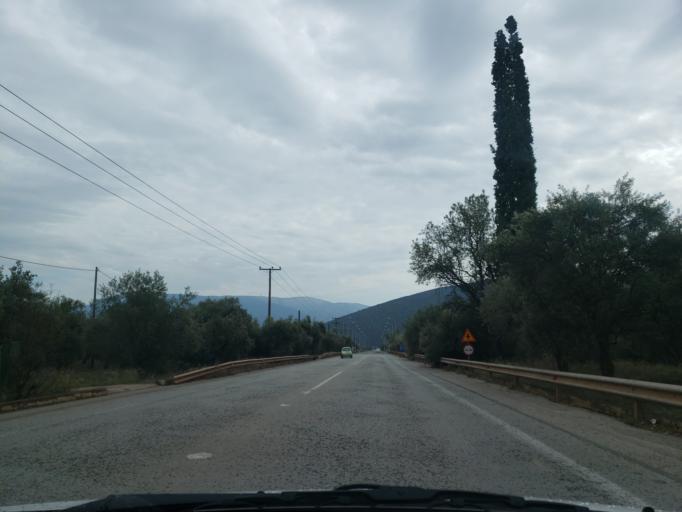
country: GR
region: Central Greece
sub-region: Nomos Fokidos
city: Amfissa
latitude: 38.4942
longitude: 22.4129
